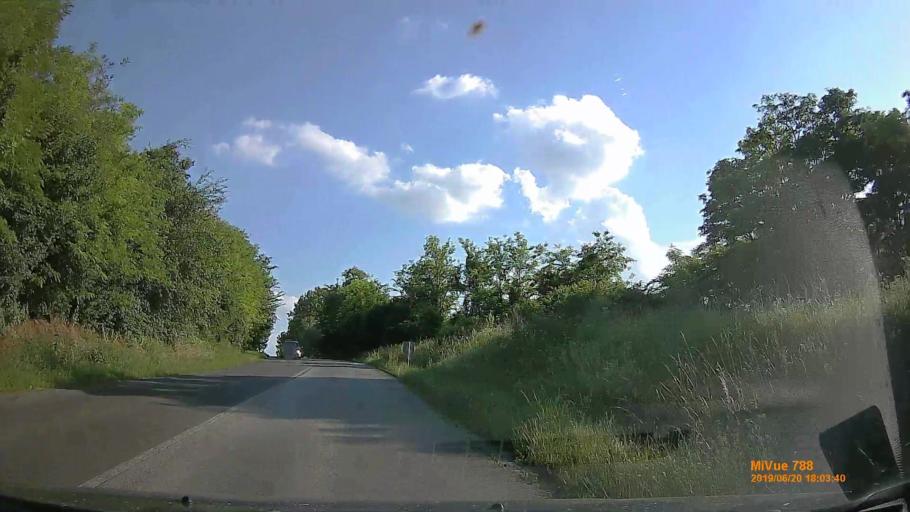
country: HU
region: Baranya
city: Szentlorinc
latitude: 46.0586
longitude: 17.9907
